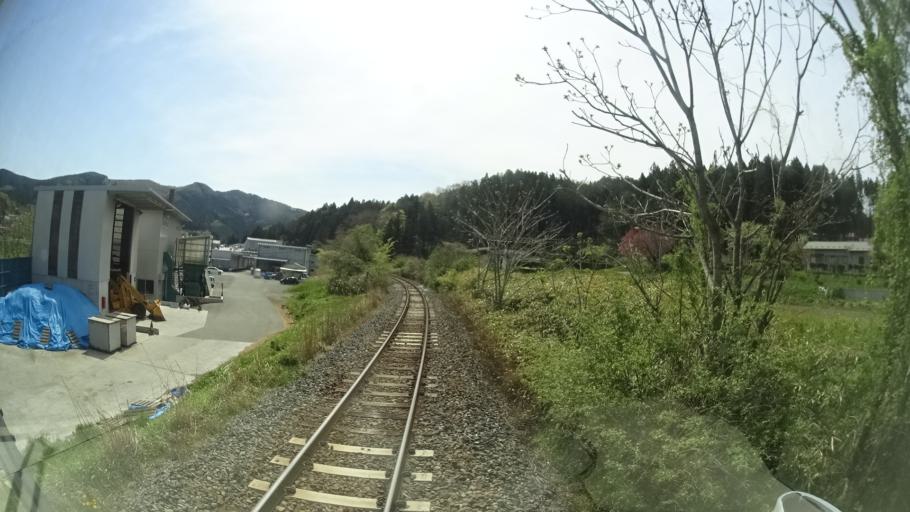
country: JP
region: Iwate
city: Ofunato
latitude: 38.9365
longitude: 141.4603
